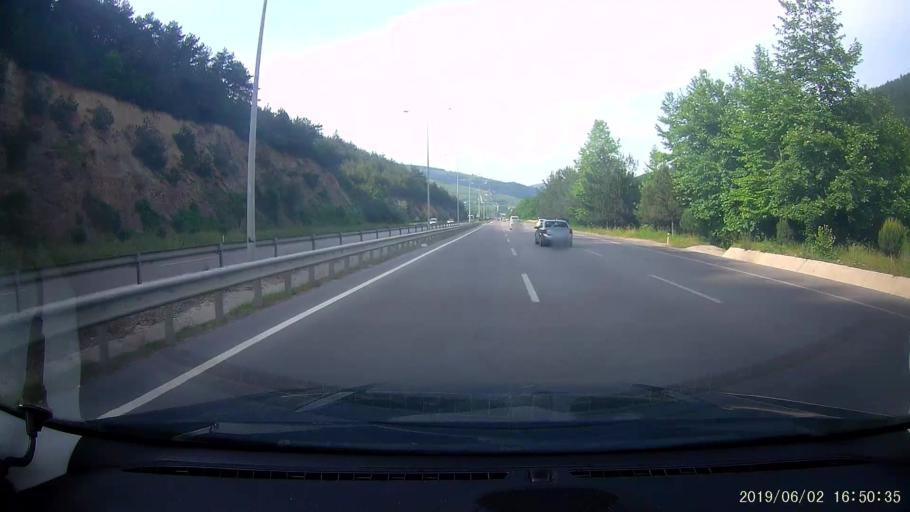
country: TR
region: Samsun
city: Taflan
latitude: 41.2578
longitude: 36.1740
